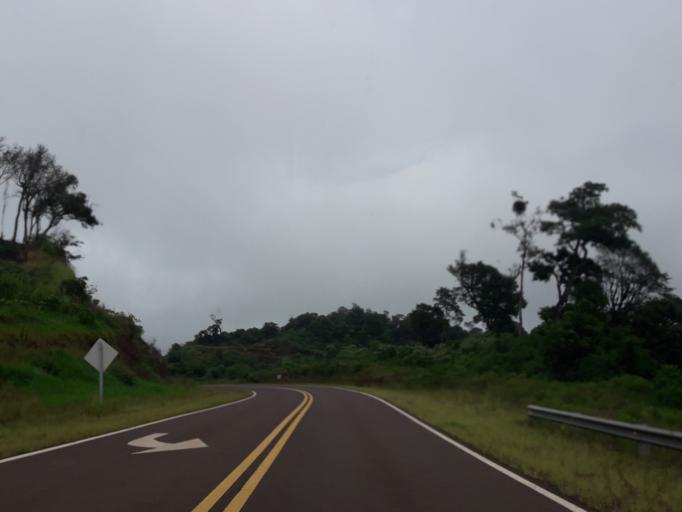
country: AR
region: Misiones
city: Bernardo de Irigoyen
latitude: -26.3996
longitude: -53.8175
